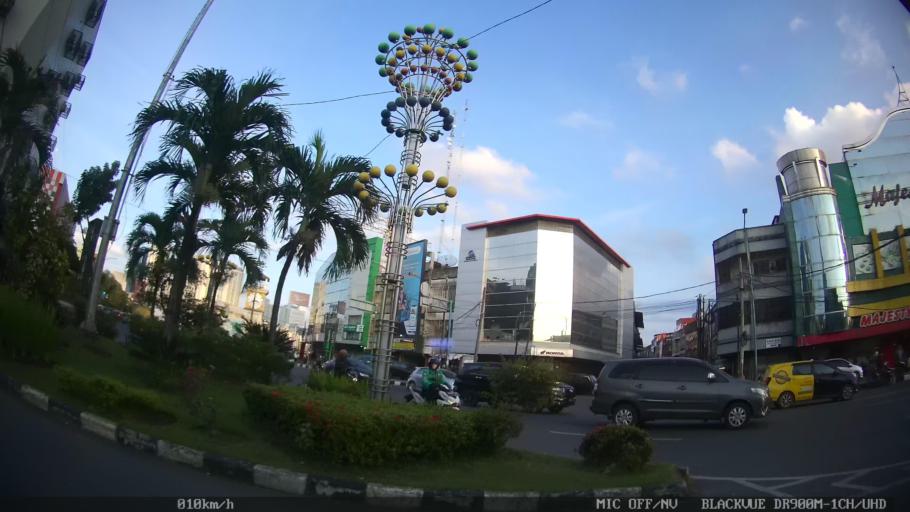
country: ID
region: North Sumatra
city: Medan
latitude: 3.5929
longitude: 98.6677
